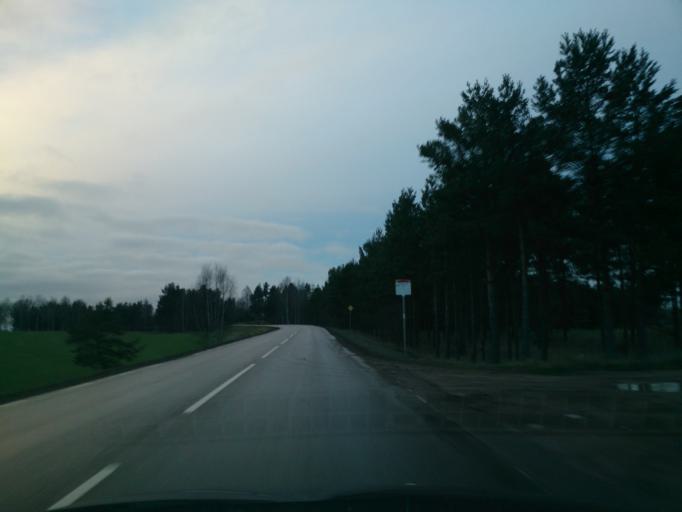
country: SE
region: OEstergoetland
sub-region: Norrkopings Kommun
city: Kimstad
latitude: 58.3984
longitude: 15.9522
